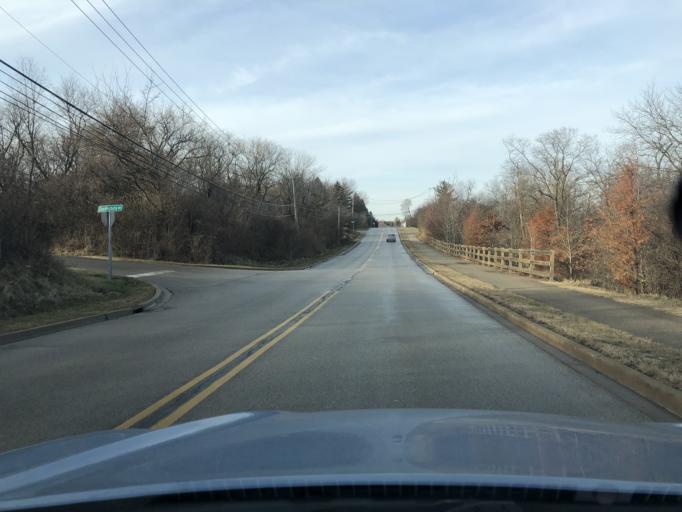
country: US
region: Illinois
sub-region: McHenry County
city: Algonquin
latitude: 42.1574
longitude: -88.3117
